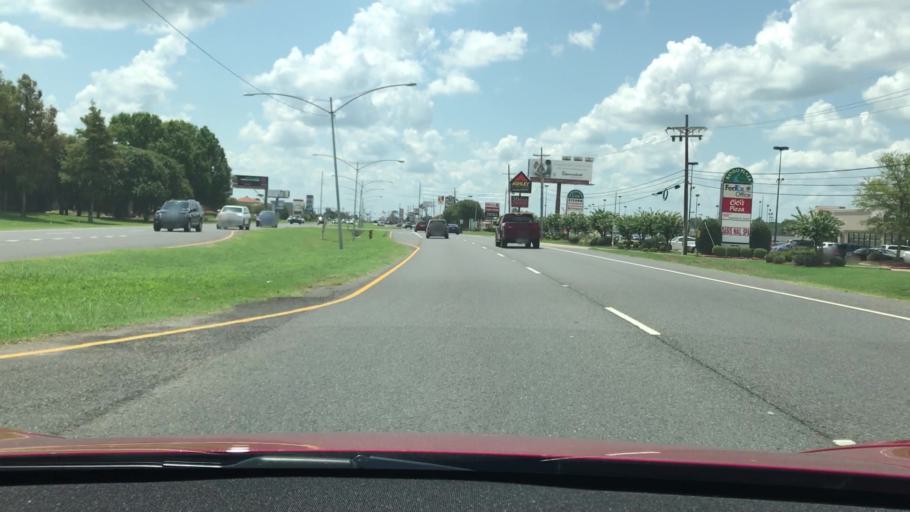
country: US
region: Louisiana
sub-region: Bossier Parish
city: Bossier City
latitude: 32.4485
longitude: -93.7216
